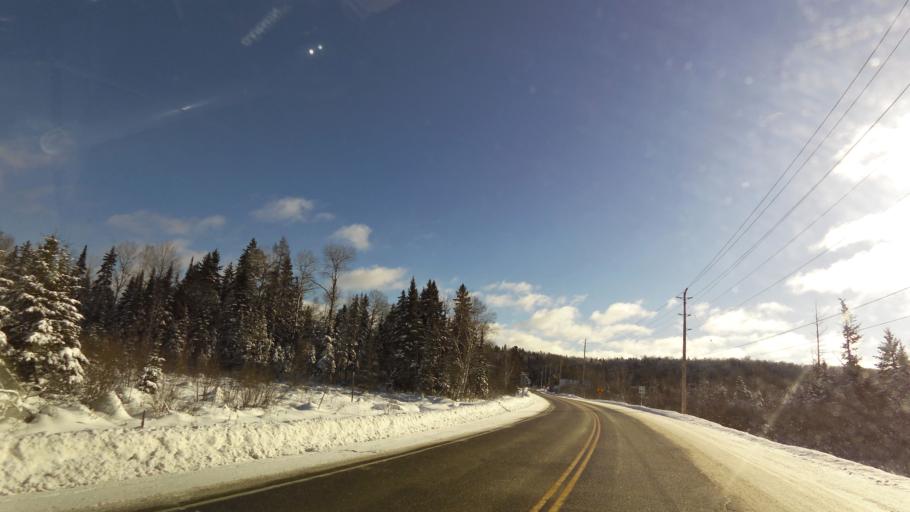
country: CA
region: Ontario
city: Bancroft
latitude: 44.9753
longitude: -78.2785
